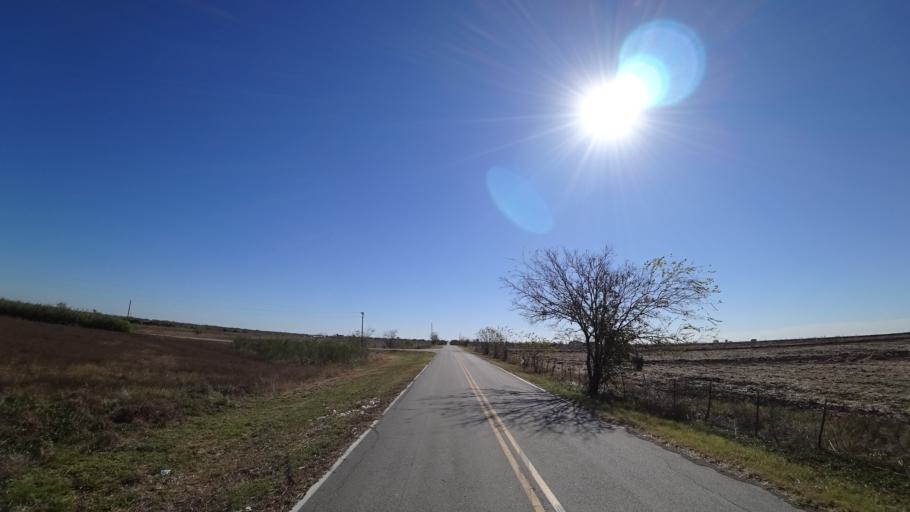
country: US
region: Texas
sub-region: Travis County
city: Garfield
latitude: 30.0990
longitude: -97.6366
